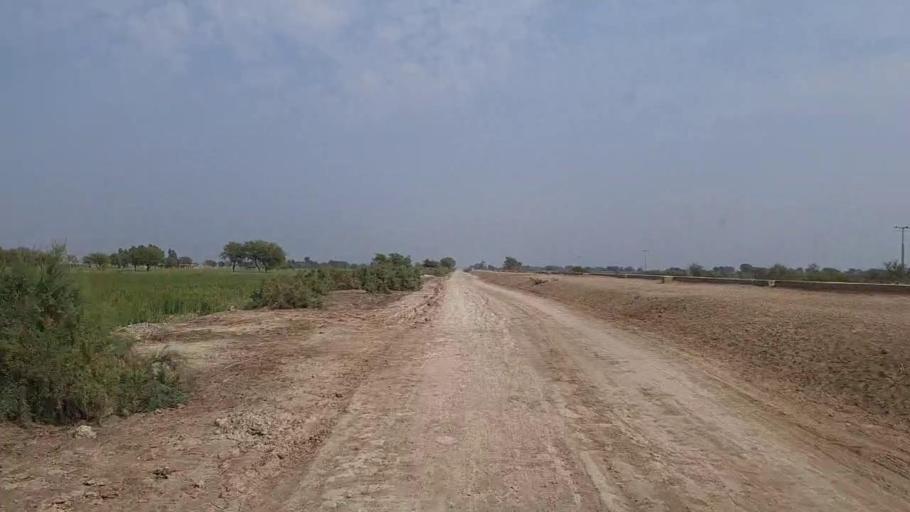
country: PK
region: Sindh
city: Mirwah Gorchani
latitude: 25.3979
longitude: 69.0977
